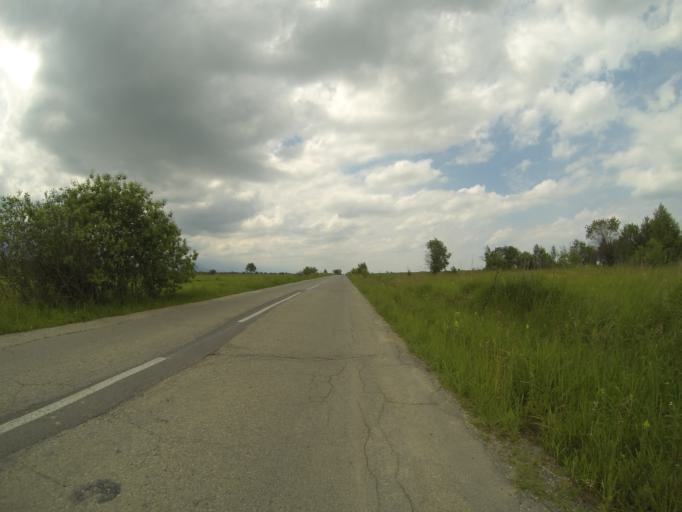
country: RO
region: Brasov
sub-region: Comuna Harseni
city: Harseni
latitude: 45.7369
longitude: 25.0722
